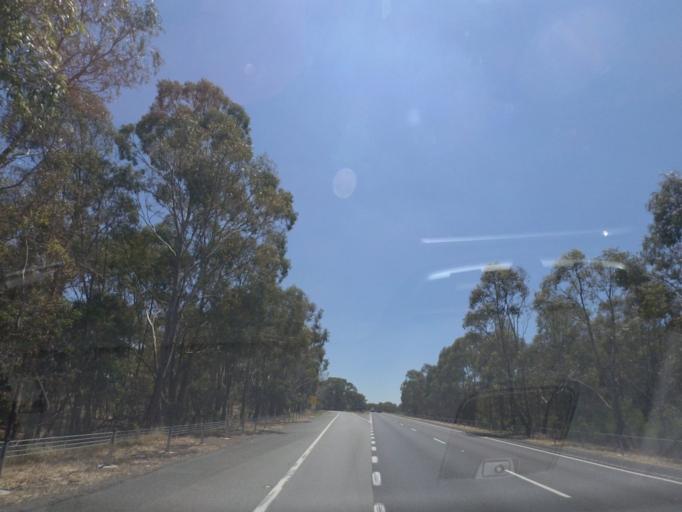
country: AU
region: Victoria
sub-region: Murrindindi
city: Kinglake West
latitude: -36.9660
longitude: 145.1798
